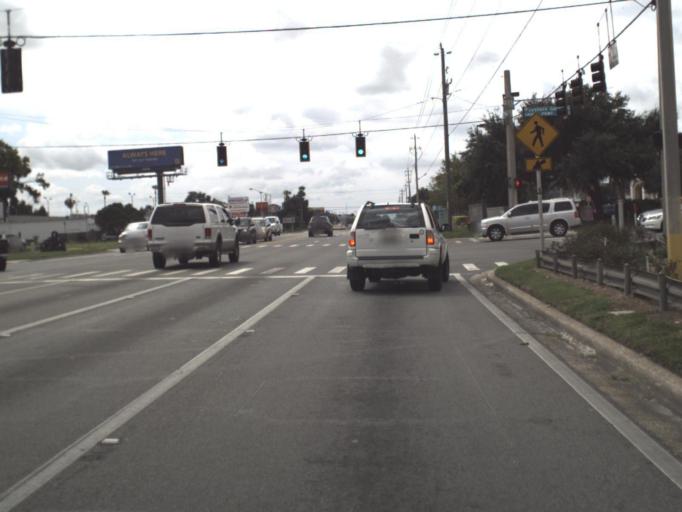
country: US
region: Florida
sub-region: Manatee County
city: Bayshore Gardens
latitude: 27.4316
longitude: -82.5756
